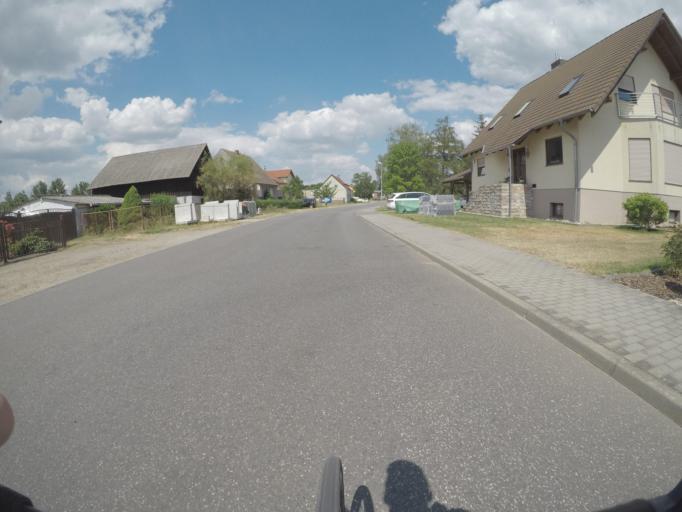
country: DE
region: Brandenburg
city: Brandenburg an der Havel
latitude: 52.4183
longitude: 12.6432
